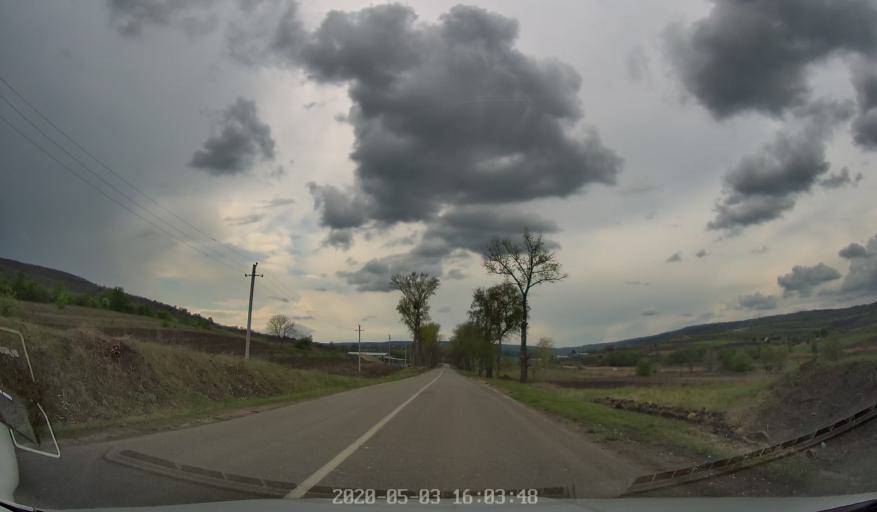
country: MD
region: Stinga Nistrului
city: Bucovat
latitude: 47.1824
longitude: 28.3764
